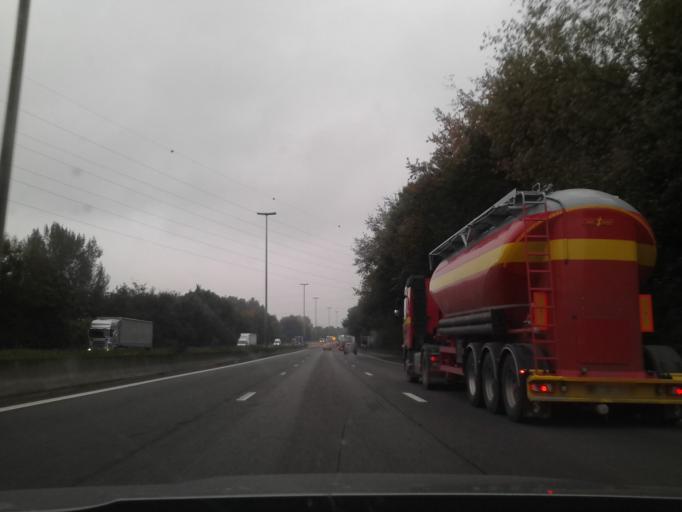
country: BE
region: Wallonia
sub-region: Province du Hainaut
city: Mons
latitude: 50.4713
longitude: 3.9349
